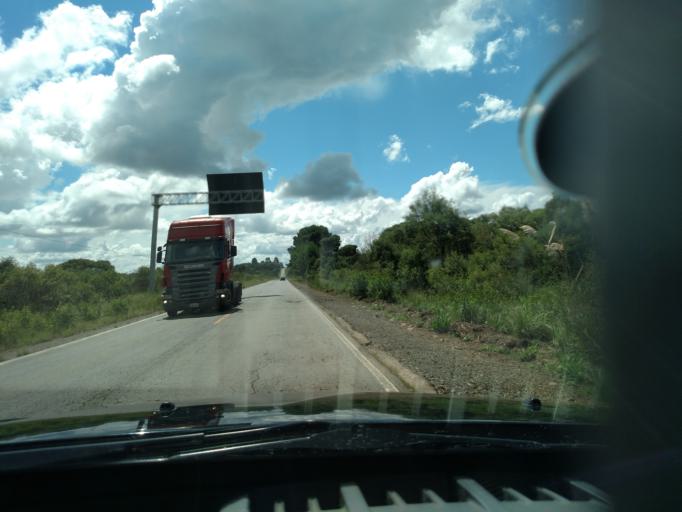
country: BR
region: Santa Catarina
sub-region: Lages
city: Lages
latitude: -27.8566
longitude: -50.2170
